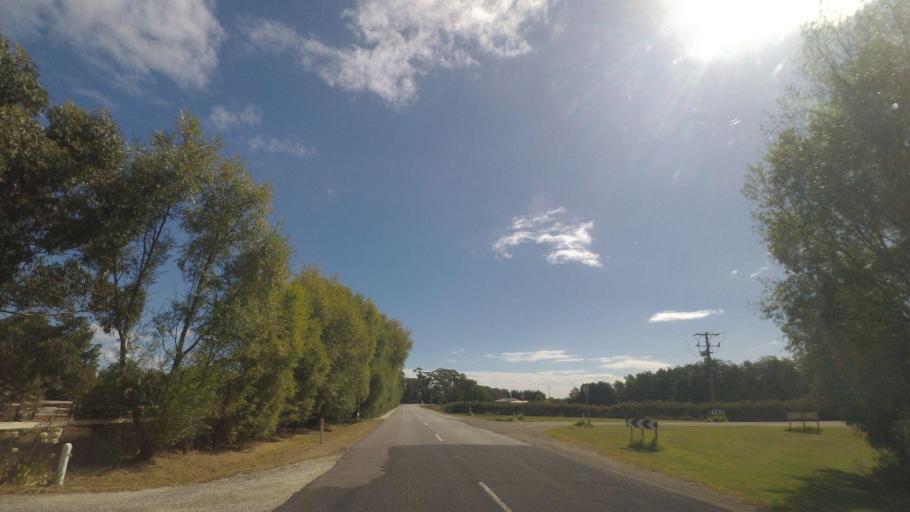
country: AU
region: Victoria
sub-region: Cardinia
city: Pakenham South
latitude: -38.1808
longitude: 145.5777
